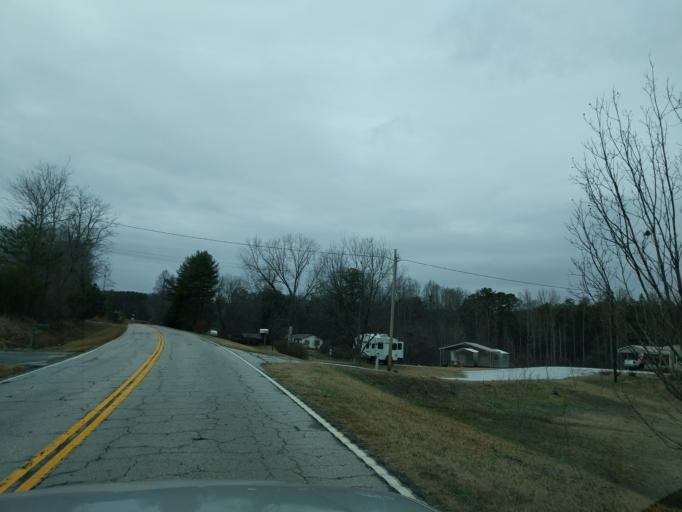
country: US
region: South Carolina
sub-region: Oconee County
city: Walhalla
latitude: 34.7842
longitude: -83.1101
